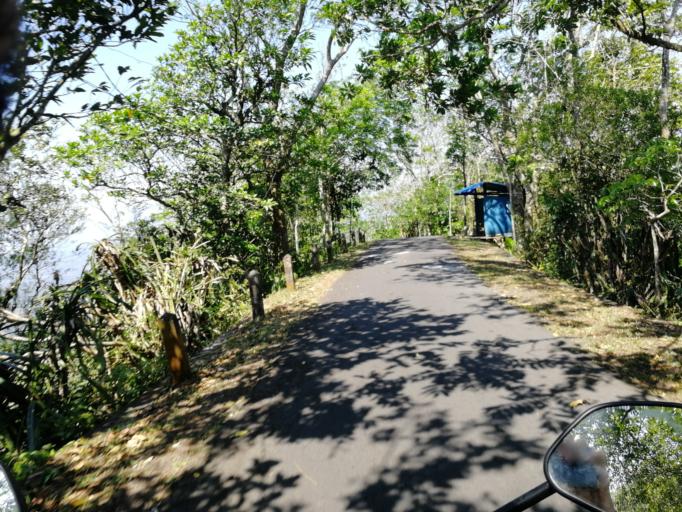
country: ID
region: Bali
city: Tiyingtali Kelod
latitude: -8.3913
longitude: 115.6380
